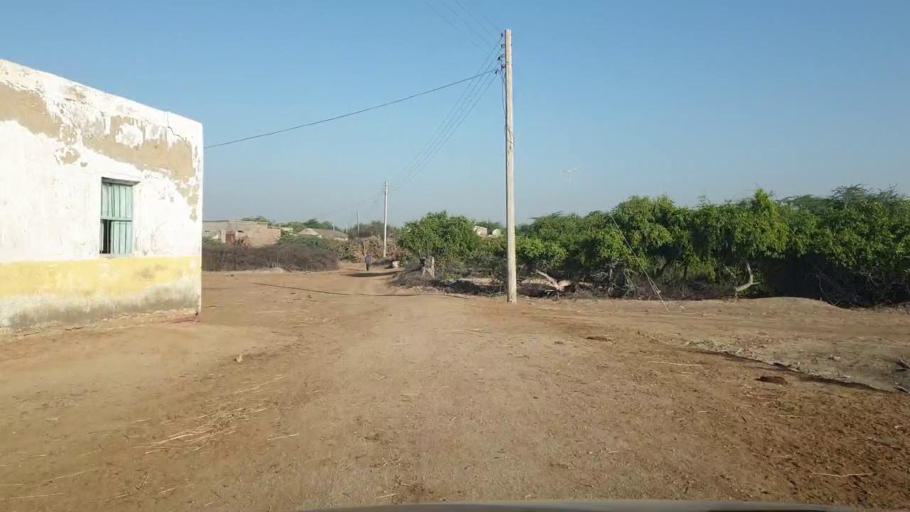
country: PK
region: Sindh
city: Badin
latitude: 24.7015
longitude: 68.8151
